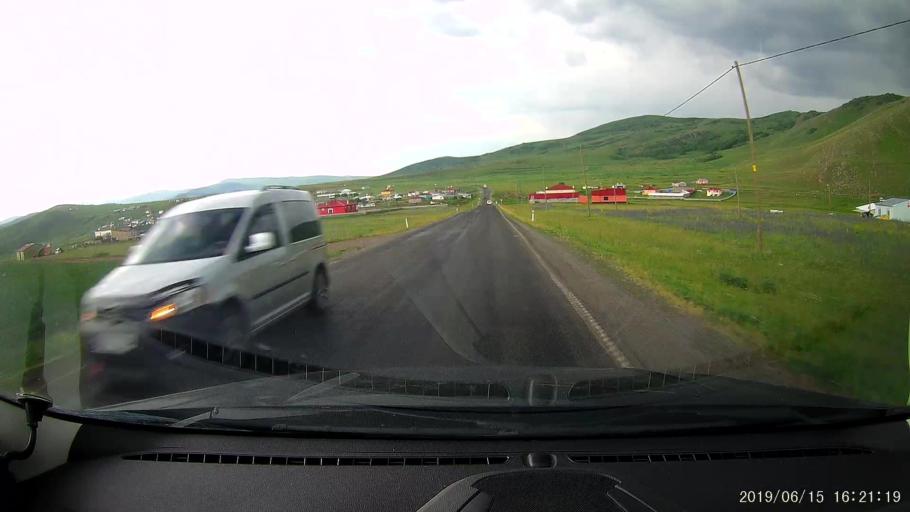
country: TR
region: Ardahan
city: Hanak
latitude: 41.2001
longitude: 42.8460
